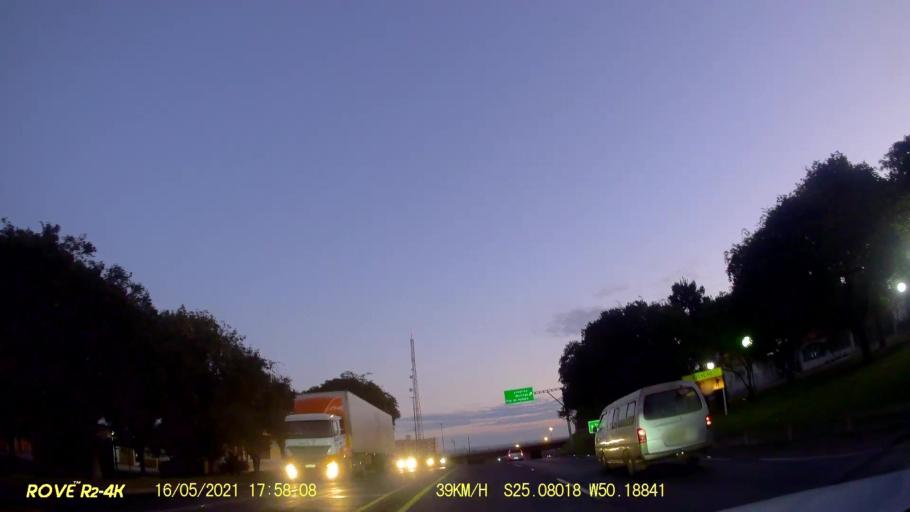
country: BR
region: Parana
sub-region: Ponta Grossa
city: Ponta Grossa
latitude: -25.0800
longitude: -50.1883
